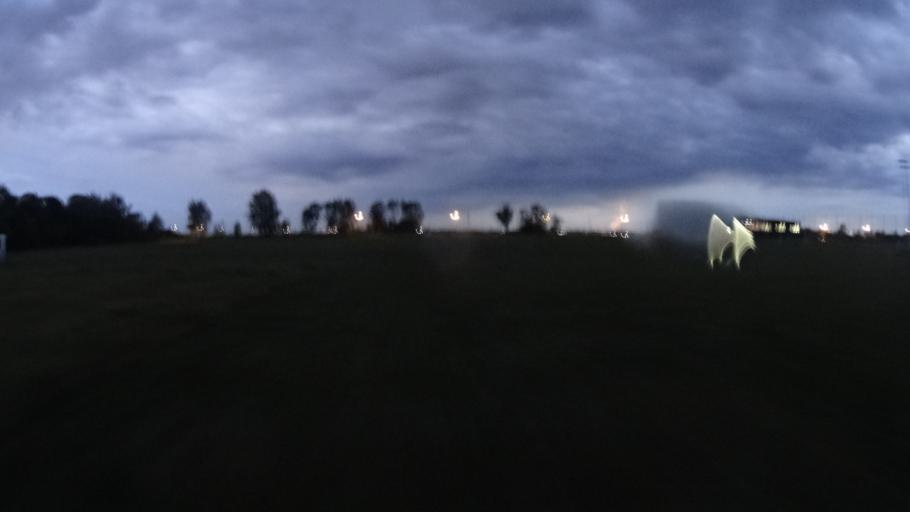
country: PL
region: Masovian Voivodeship
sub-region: Powiat warszawski zachodni
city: Ozarow Mazowiecki
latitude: 52.2326
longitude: 20.8002
